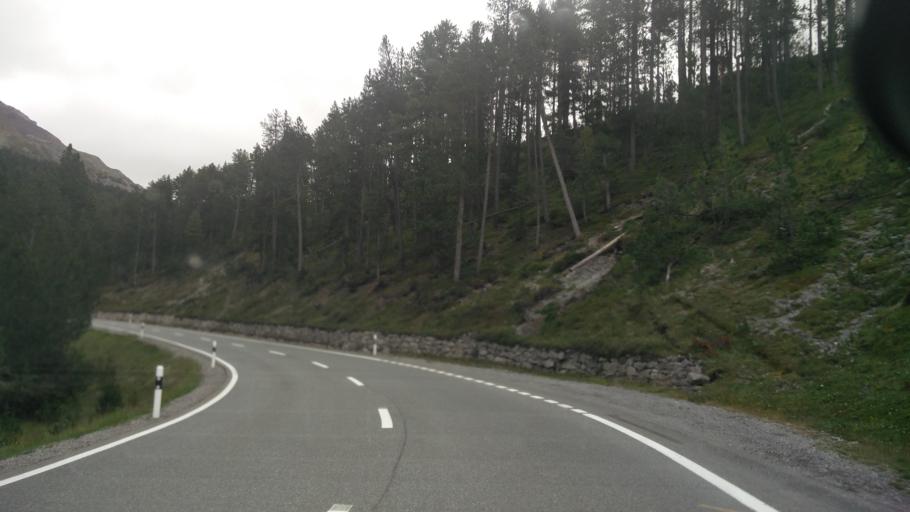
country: CH
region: Grisons
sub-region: Inn District
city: Scuol
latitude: 46.6461
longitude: 10.2719
